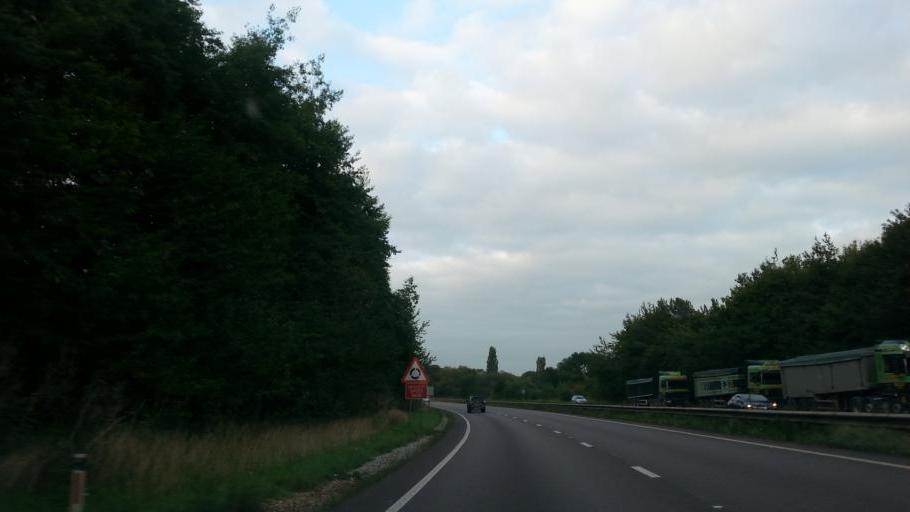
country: GB
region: England
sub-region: Northamptonshire
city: Brackley
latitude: 52.0219
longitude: -1.1400
